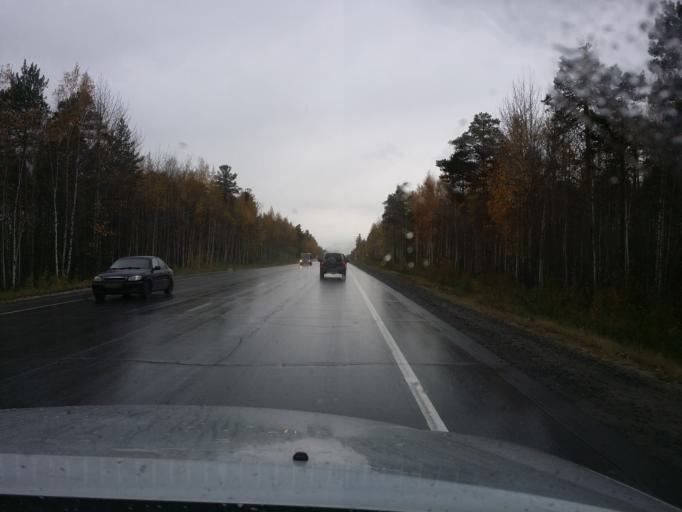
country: RU
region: Khanty-Mansiyskiy Avtonomnyy Okrug
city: Megion
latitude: 61.0563
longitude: 76.3017
